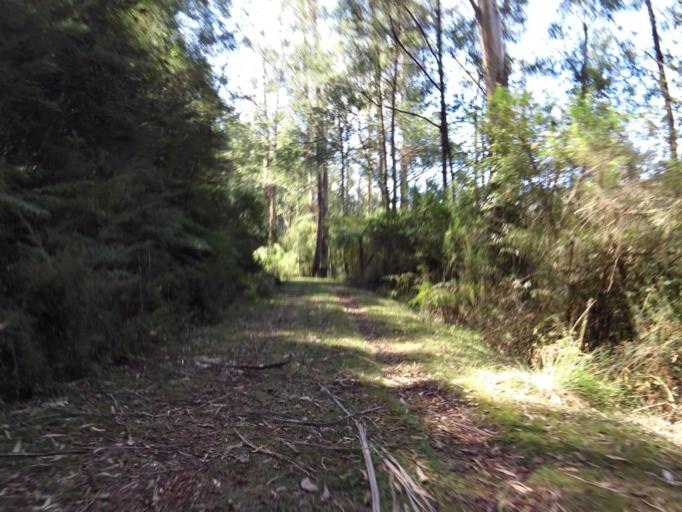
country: AU
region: Victoria
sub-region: Yarra Ranges
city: Millgrove
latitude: -37.6955
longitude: 145.8011
